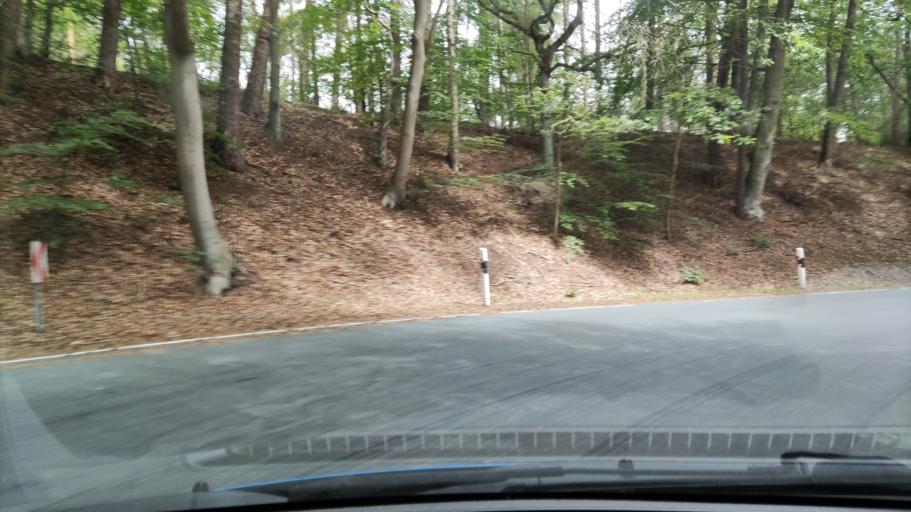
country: DE
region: Lower Saxony
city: Clenze
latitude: 52.9309
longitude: 10.9137
